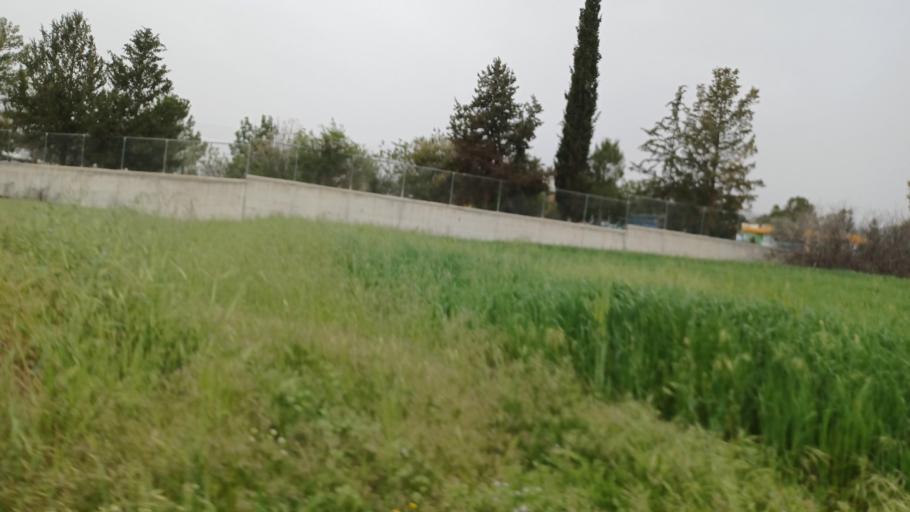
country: CY
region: Limassol
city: Parekklisha
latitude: 34.8467
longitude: 33.1449
